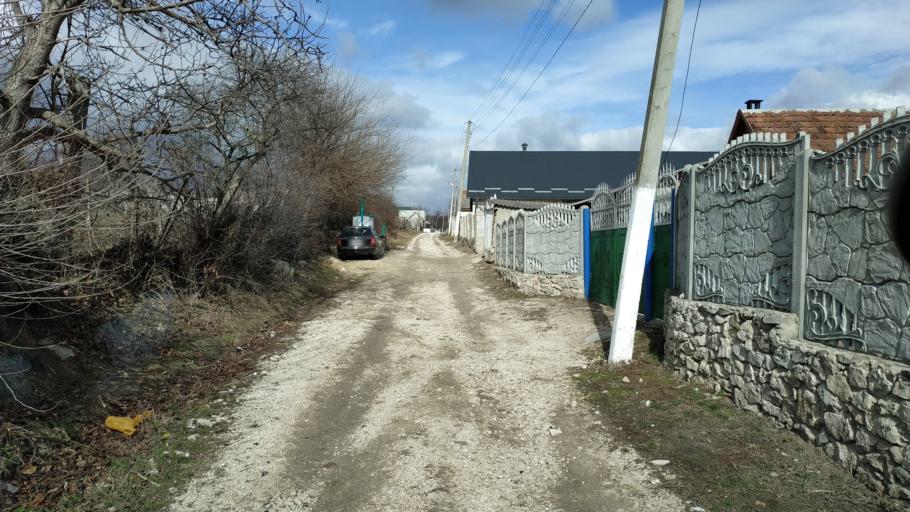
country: MD
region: Stinga Nistrului
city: Bucovat
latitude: 47.2088
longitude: 28.4966
